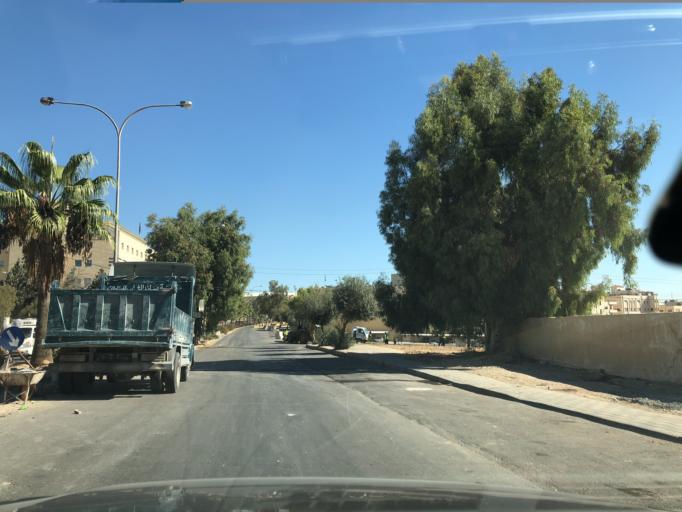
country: JO
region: Amman
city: Amman
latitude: 31.9770
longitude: 35.9051
